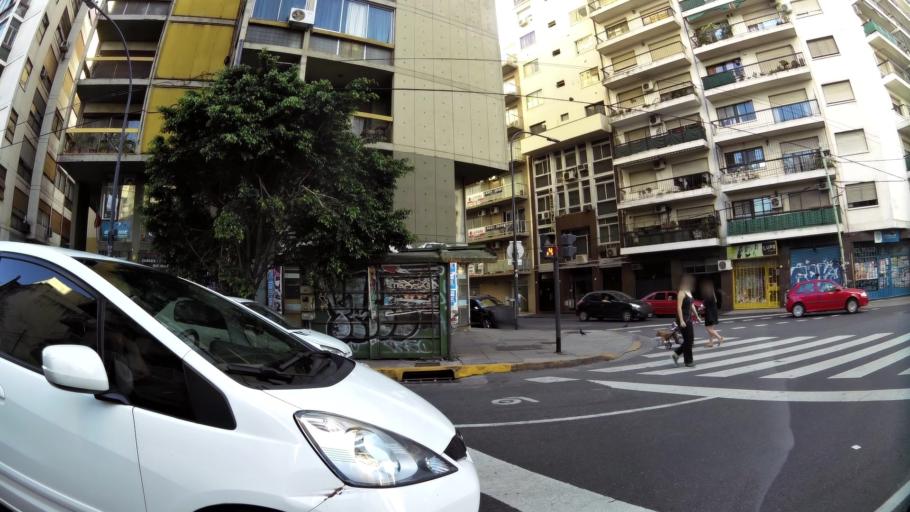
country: AR
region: Buenos Aires F.D.
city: Retiro
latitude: -34.5992
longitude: -58.4023
